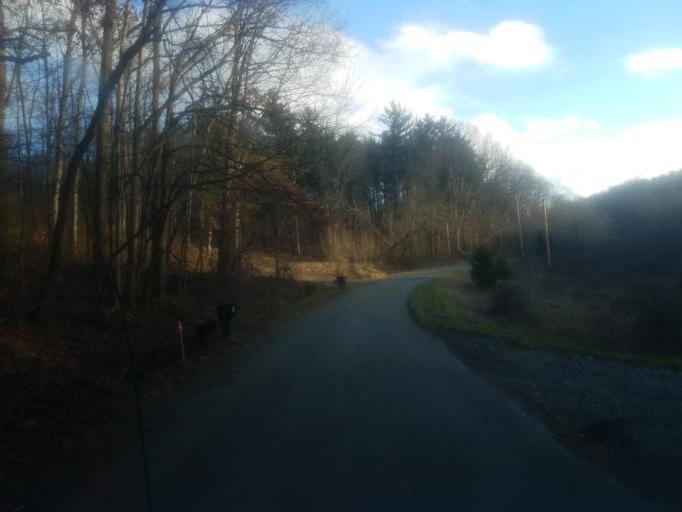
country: US
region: Ohio
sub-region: Sandusky County
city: Bellville
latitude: 40.5940
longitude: -82.3910
